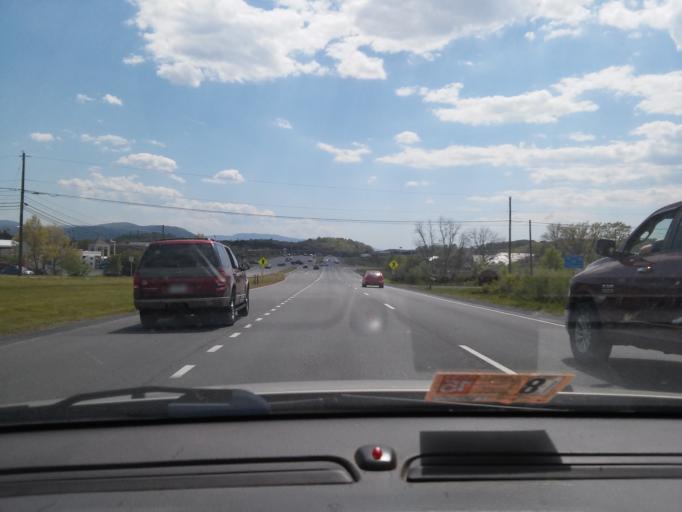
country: US
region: Virginia
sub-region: Warren County
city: Front Royal
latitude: 38.9684
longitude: -78.1884
